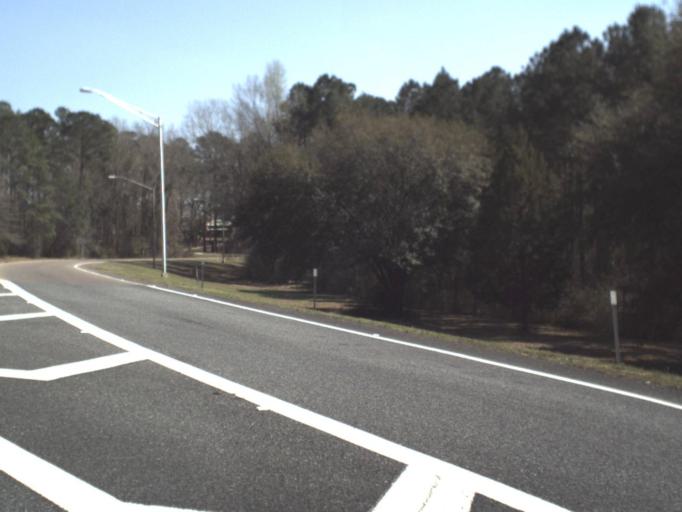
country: US
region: Florida
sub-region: Jackson County
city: Marianna
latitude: 30.7571
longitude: -85.3311
